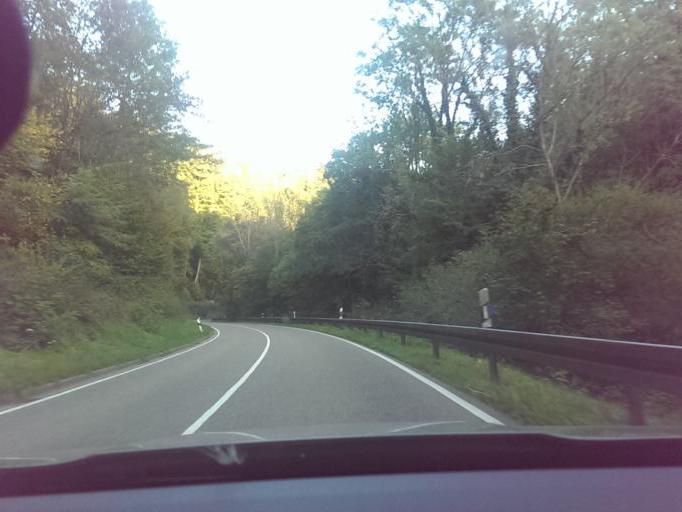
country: DE
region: Baden-Wuerttemberg
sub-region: Karlsruhe Region
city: Unterreichenbach
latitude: 48.8435
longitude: 8.7447
